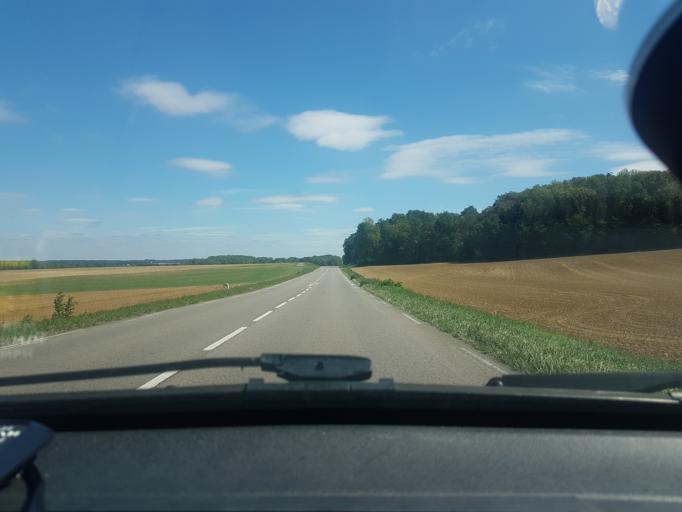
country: FR
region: Bourgogne
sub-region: Departement de la Cote-d'Or
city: Mirebeau-sur-Beze
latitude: 47.4053
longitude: 5.3626
